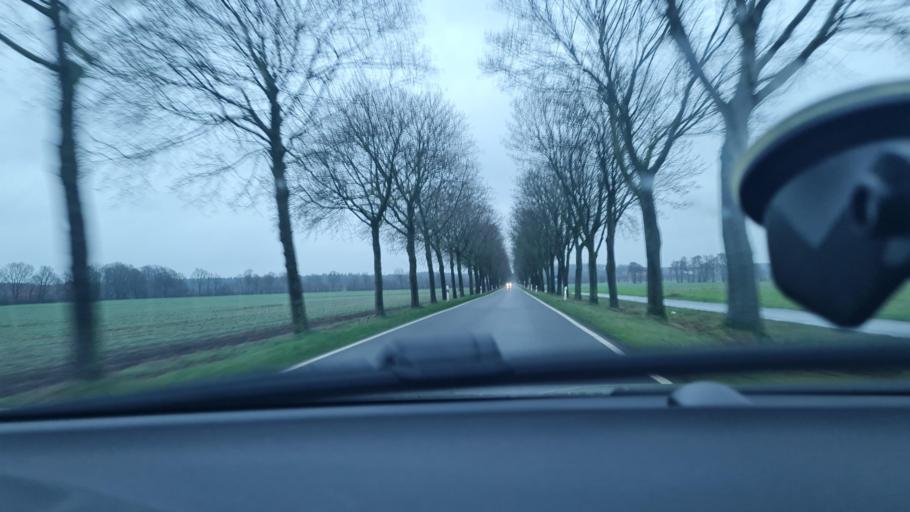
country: DE
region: North Rhine-Westphalia
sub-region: Regierungsbezirk Munster
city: Heiden
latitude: 51.7747
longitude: 6.9207
